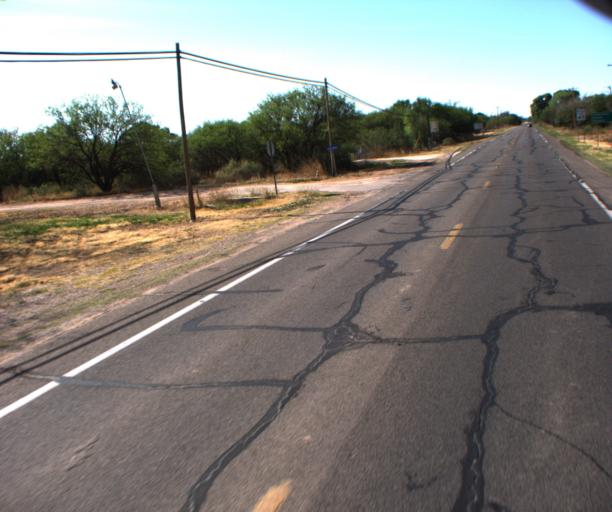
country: US
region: Arizona
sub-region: Cochise County
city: Saint David
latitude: 31.8989
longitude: -110.2135
